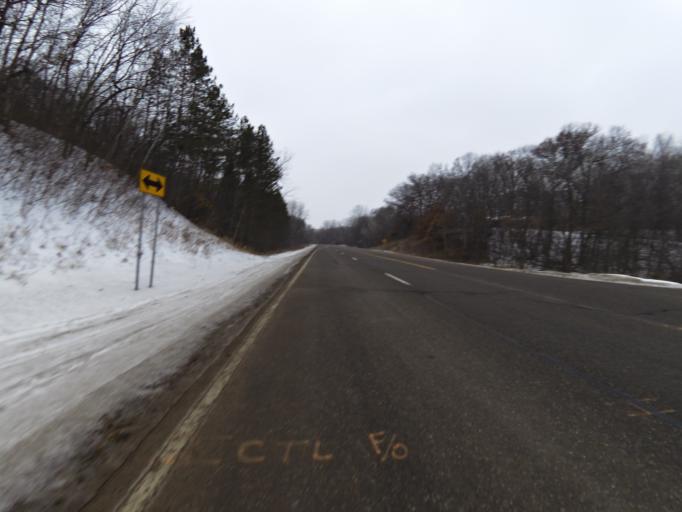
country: US
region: Minnesota
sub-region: Washington County
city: Lake Elmo
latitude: 44.9639
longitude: -92.8369
